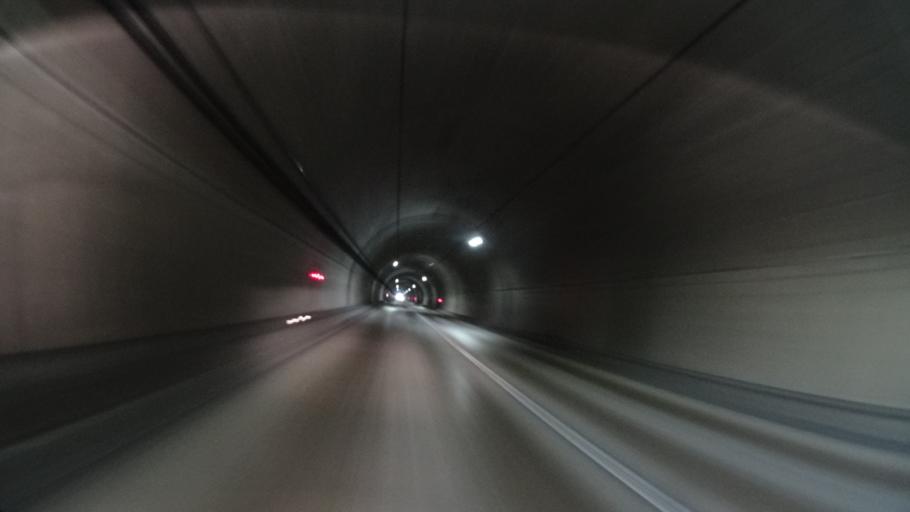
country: JP
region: Fukui
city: Maruoka
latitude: 36.1306
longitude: 136.3237
